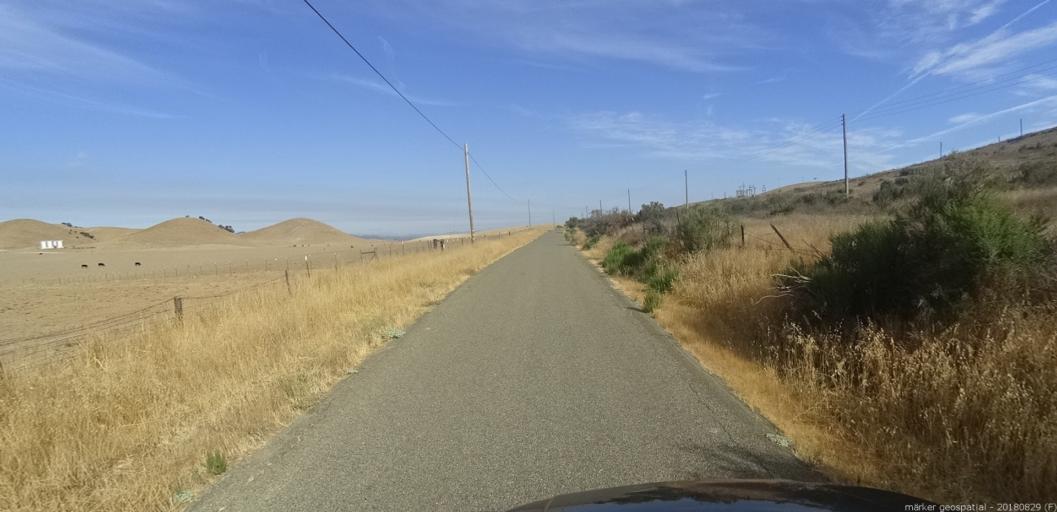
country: US
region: California
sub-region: Monterey County
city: King City
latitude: 36.0413
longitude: -120.9732
